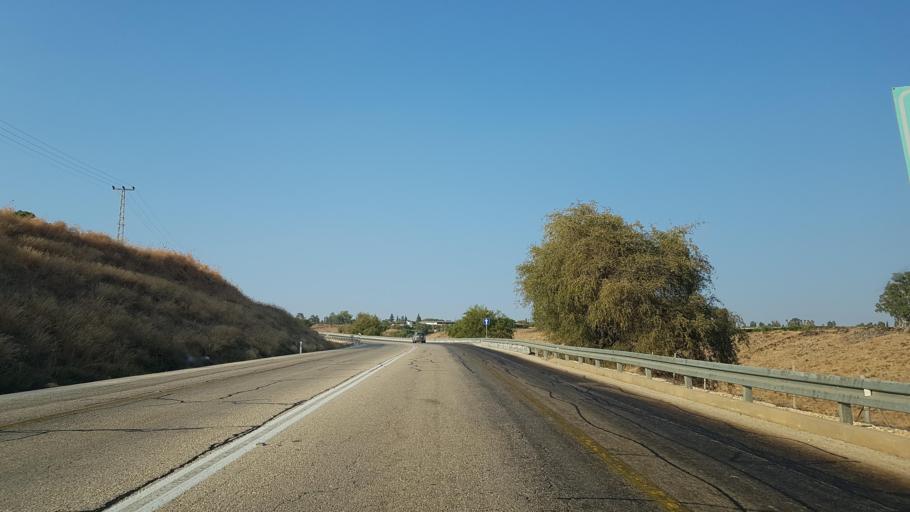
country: SY
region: Quneitra
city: Al Butayhah
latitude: 32.9013
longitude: 35.5972
